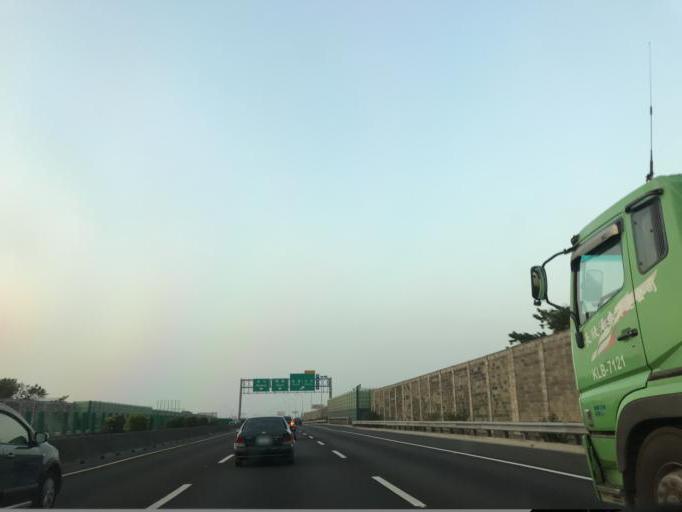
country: TW
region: Taiwan
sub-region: Yunlin
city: Douliu
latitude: 23.7250
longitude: 120.4744
